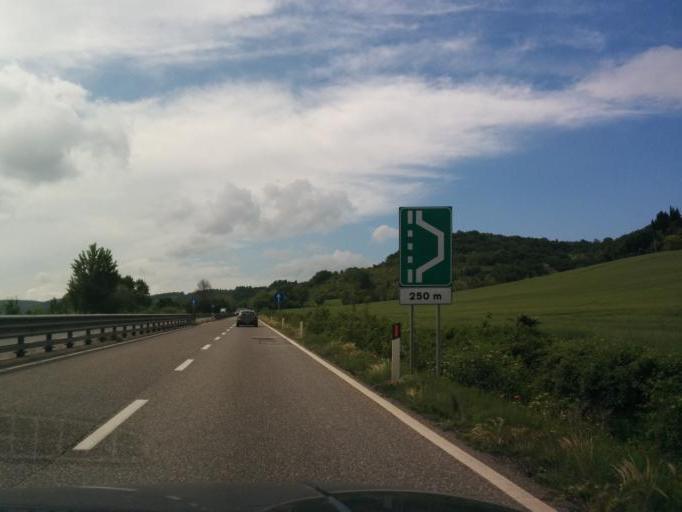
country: IT
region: Tuscany
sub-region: Province of Florence
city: Sambuca
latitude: 43.5852
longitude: 11.2019
